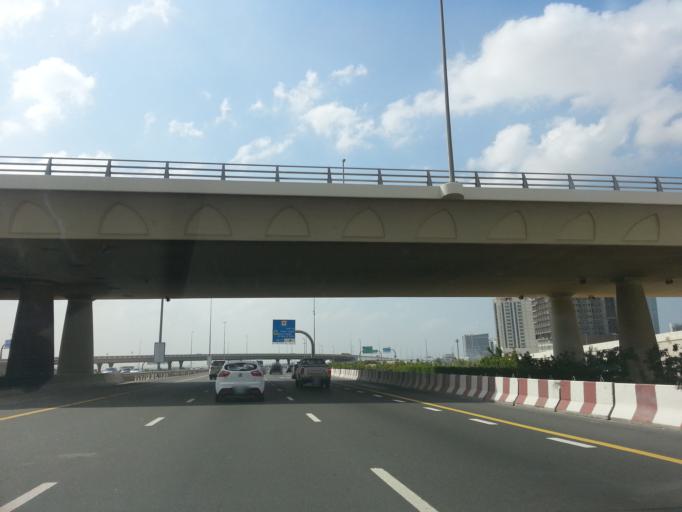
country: AE
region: Dubai
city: Dubai
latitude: 25.1856
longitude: 55.2882
